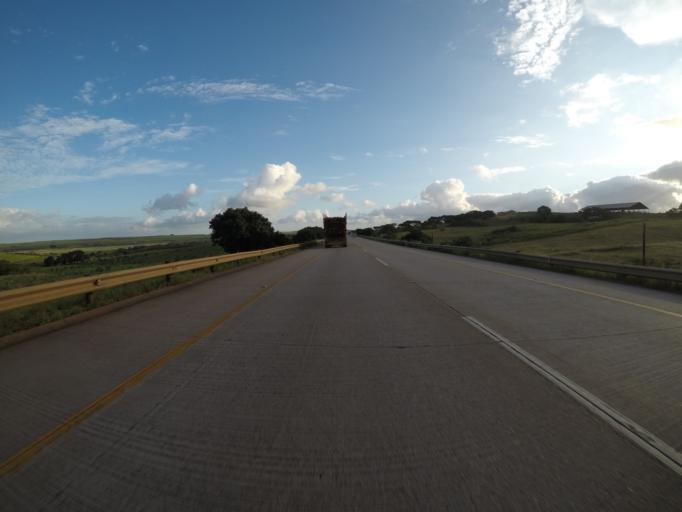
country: ZA
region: KwaZulu-Natal
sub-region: uMkhanyakude District Municipality
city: Mtubatuba
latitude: -28.4811
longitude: 32.1434
